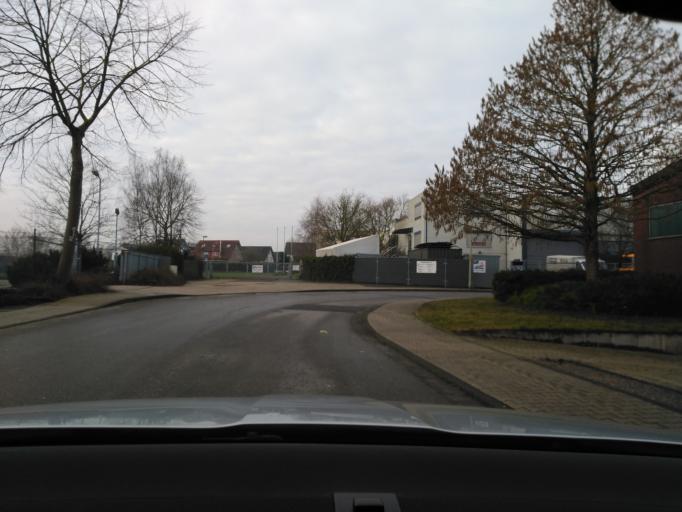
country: DE
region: North Rhine-Westphalia
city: Wegberg
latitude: 51.1469
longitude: 6.2868
